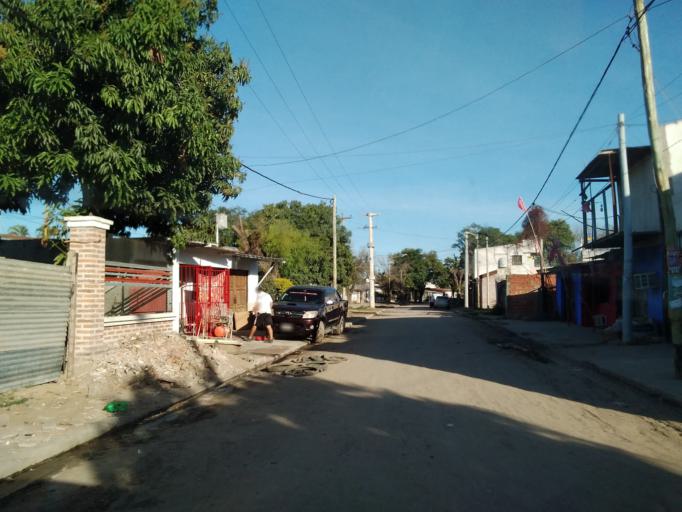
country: AR
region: Corrientes
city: Corrientes
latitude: -27.5020
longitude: -58.8362
